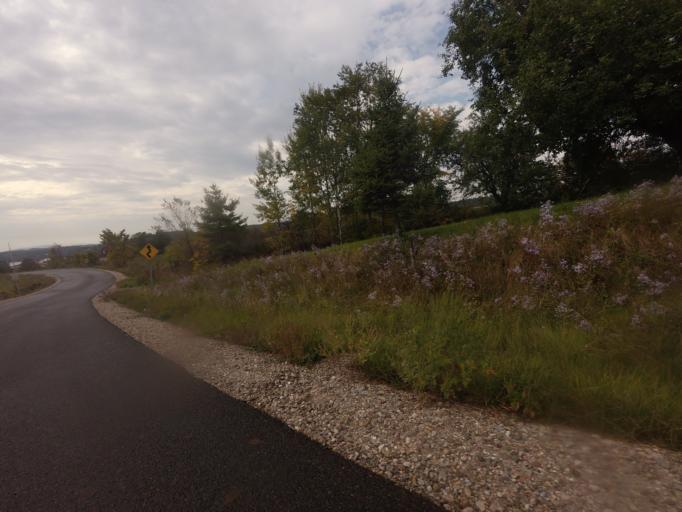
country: CA
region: Quebec
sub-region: Outaouais
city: Wakefield
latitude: 45.9823
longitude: -75.9372
